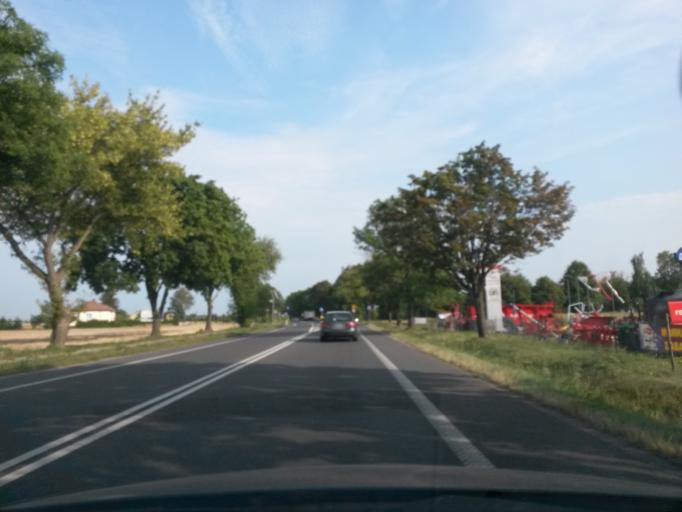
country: PL
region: Masovian Voivodeship
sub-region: Powiat sierpecki
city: Sierpc
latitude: 52.8461
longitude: 19.7133
